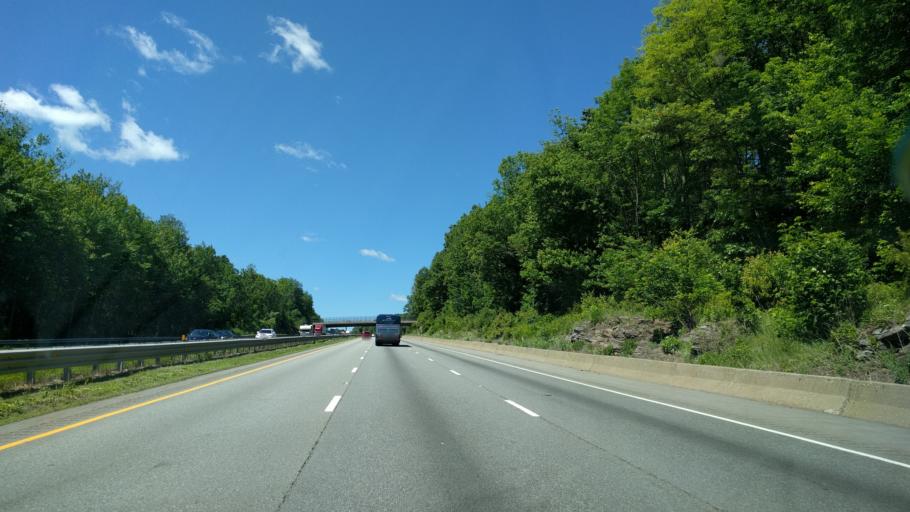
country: US
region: Massachusetts
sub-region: Worcester County
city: Charlton
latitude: 42.1615
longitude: -71.9512
